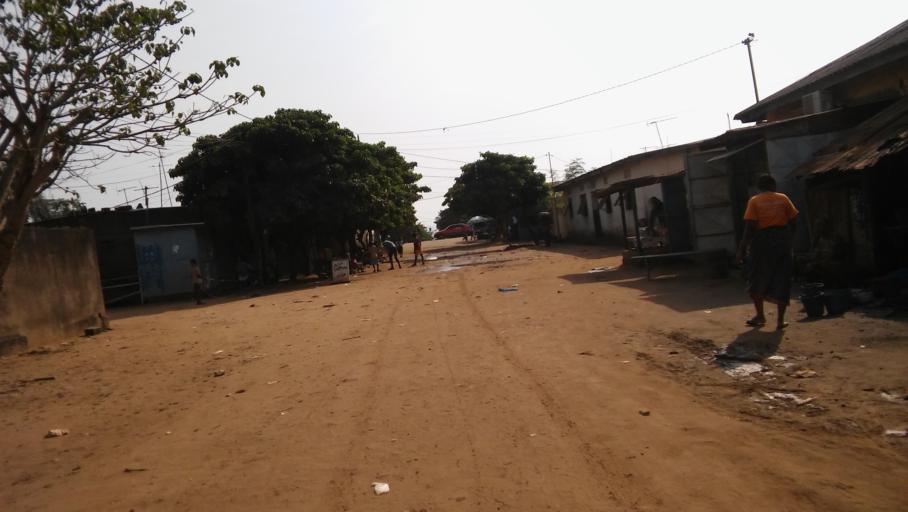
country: CI
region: Sud-Comoe
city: Grand-Bassam
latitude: 5.2064
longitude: -3.7333
